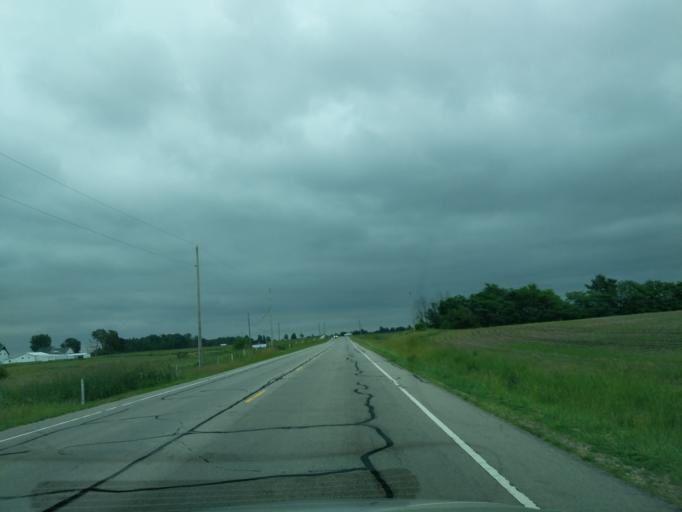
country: US
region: Indiana
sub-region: Madison County
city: Alexandria
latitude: 40.2770
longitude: -85.5998
